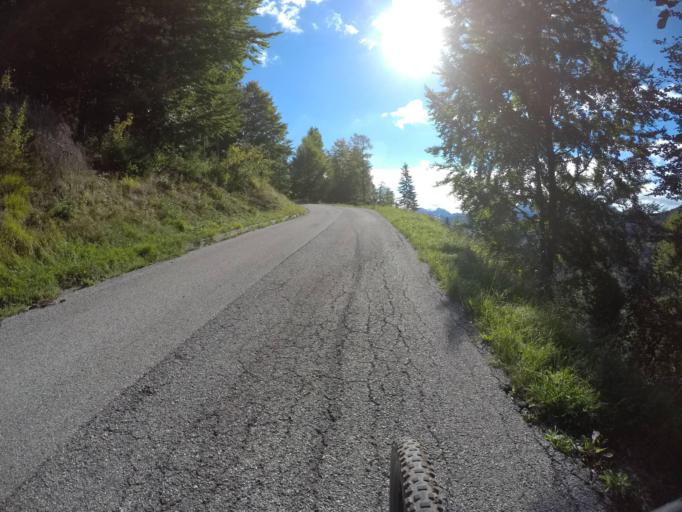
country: IT
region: Friuli Venezia Giulia
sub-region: Provincia di Udine
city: Ligosullo
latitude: 46.5444
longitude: 13.0819
